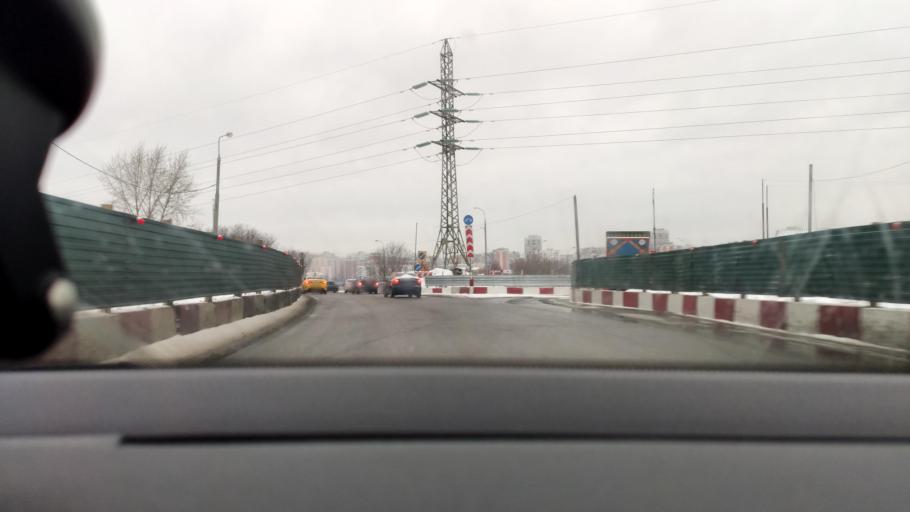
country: RU
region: Moscow
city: Kapotnya
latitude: 55.6589
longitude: 37.7910
